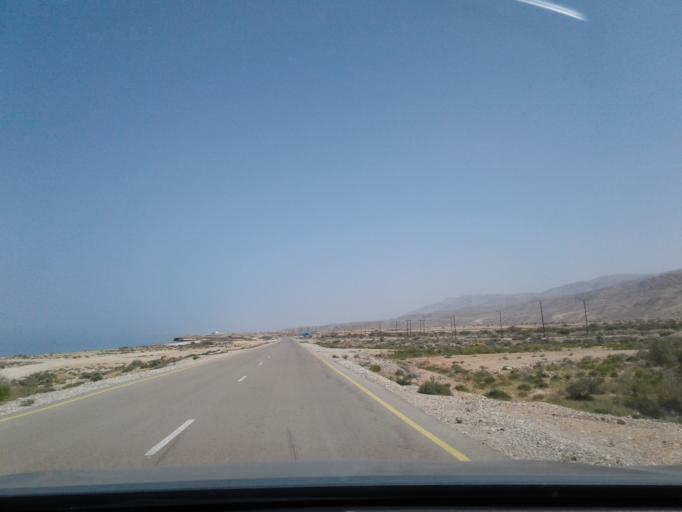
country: OM
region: Ash Sharqiyah
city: Al Qabil
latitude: 23.0364
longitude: 59.0781
